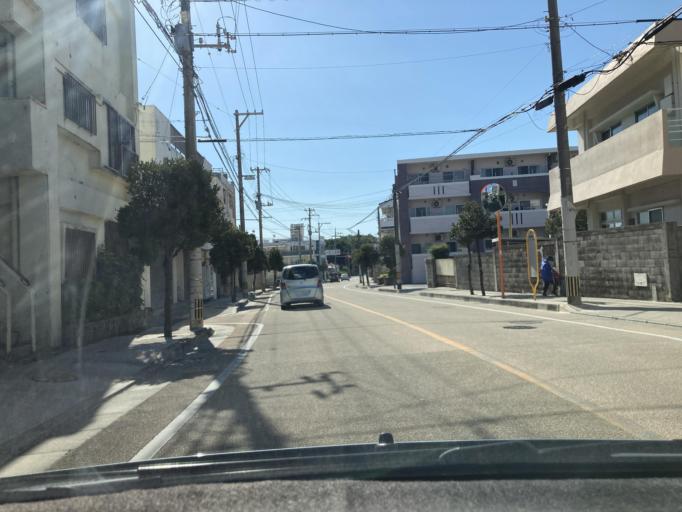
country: JP
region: Okinawa
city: Naha-shi
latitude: 26.2066
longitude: 127.7149
